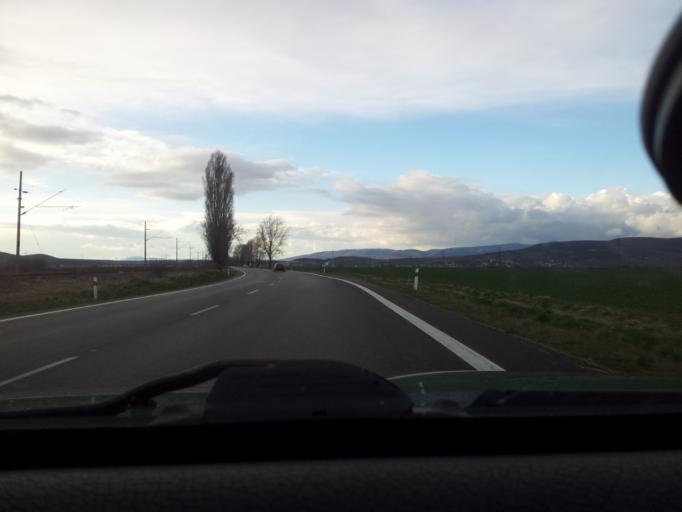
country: SK
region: Nitriansky
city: Levice
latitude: 48.2569
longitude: 18.5756
